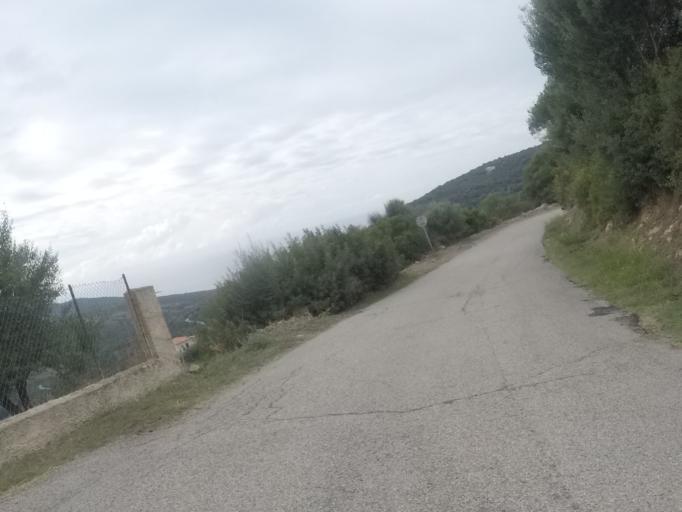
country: FR
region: Corsica
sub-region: Departement de la Corse-du-Sud
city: Pietrosella
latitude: 41.7548
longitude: 8.8142
